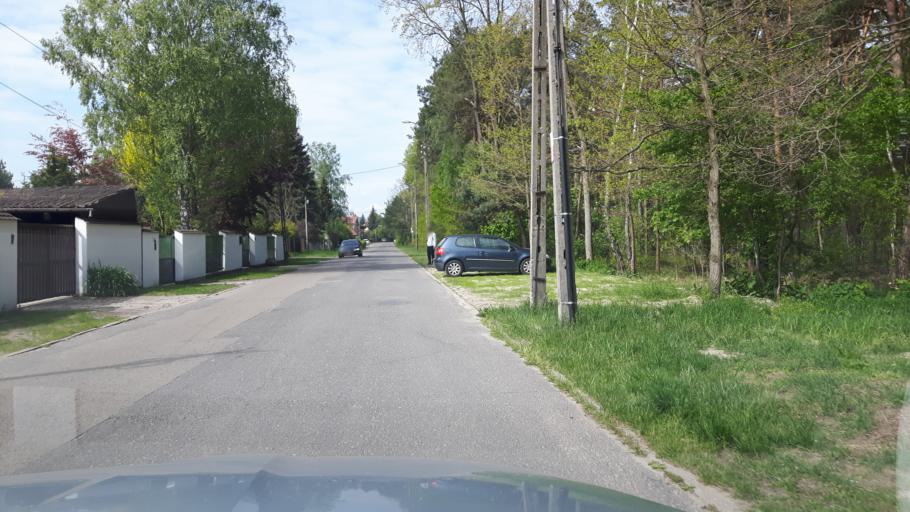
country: PL
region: Masovian Voivodeship
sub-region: Warszawa
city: Wesola
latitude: 52.2510
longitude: 21.1948
